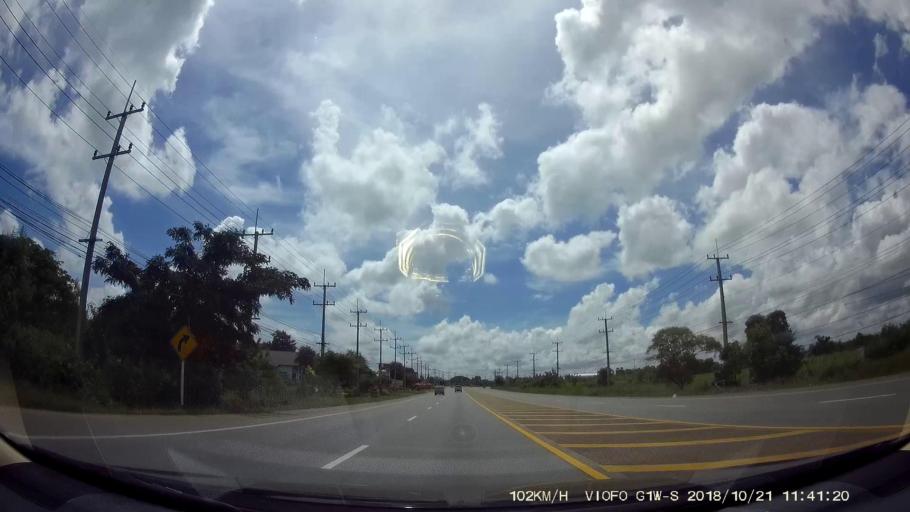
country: TH
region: Chaiyaphum
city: Chaiyaphum
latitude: 15.7004
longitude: 102.0147
